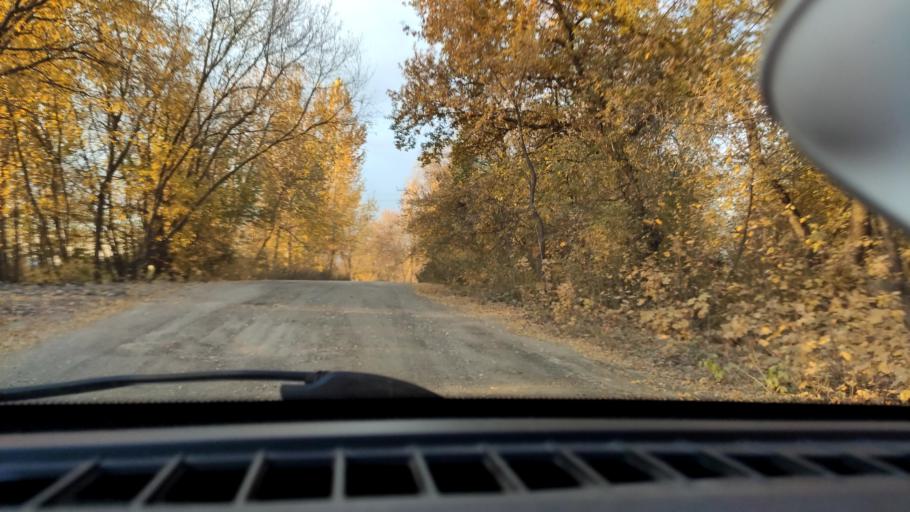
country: RU
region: Samara
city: Samara
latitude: 53.2706
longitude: 50.2303
